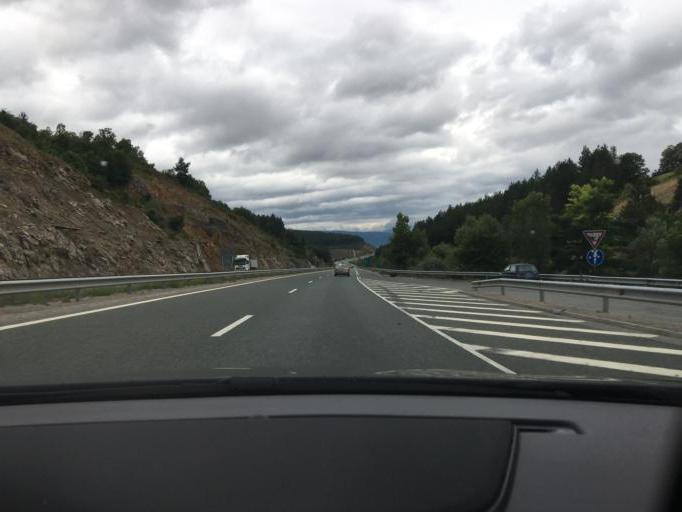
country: BG
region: Pernik
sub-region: Obshtina Pernik
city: Pernik
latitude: 42.4915
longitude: 23.1321
